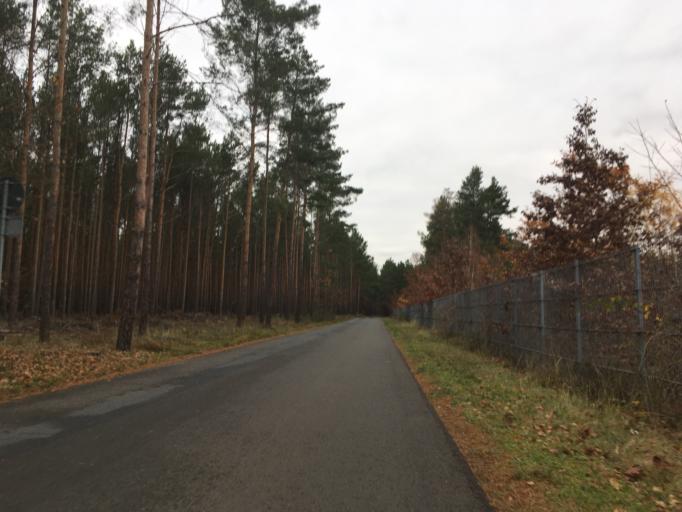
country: DE
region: Brandenburg
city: Mullrose
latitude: 52.2685
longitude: 14.4785
